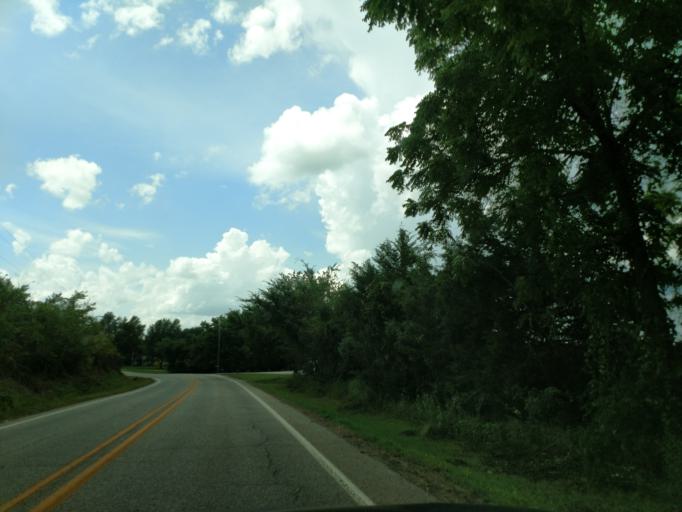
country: US
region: Arkansas
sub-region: Boone County
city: Harrison
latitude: 36.2499
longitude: -93.2147
